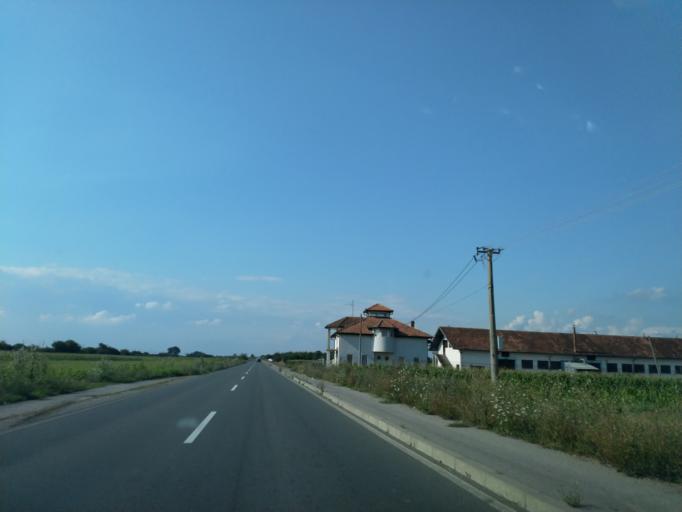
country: RS
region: Central Serbia
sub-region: Pomoravski Okrug
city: Paracin
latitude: 43.8072
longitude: 21.4210
